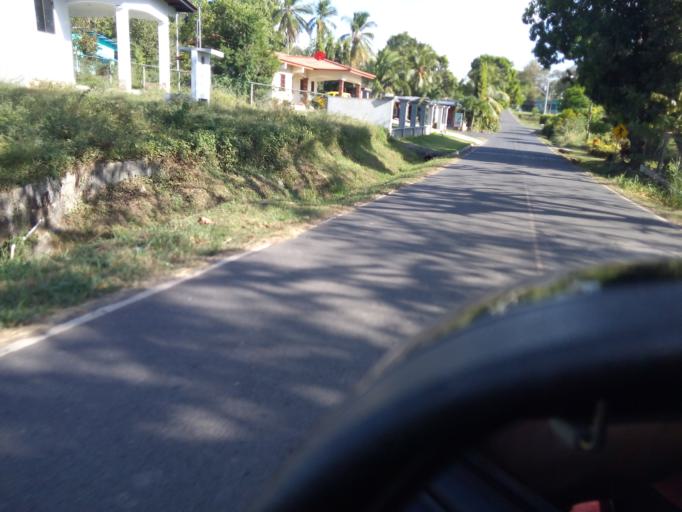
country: PA
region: Veraguas
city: Atalaya
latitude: 8.0412
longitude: -80.9256
